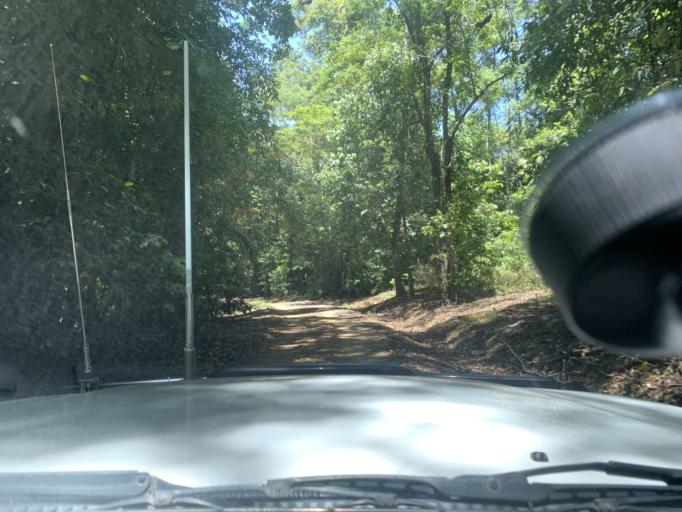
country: AU
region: Queensland
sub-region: Cairns
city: Redlynch
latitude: -16.9688
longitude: 145.6491
